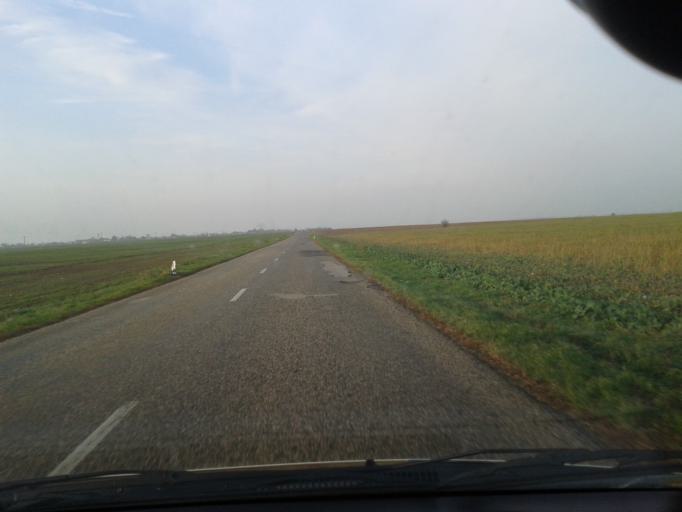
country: SK
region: Nitriansky
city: Levice
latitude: 48.1225
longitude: 18.5295
